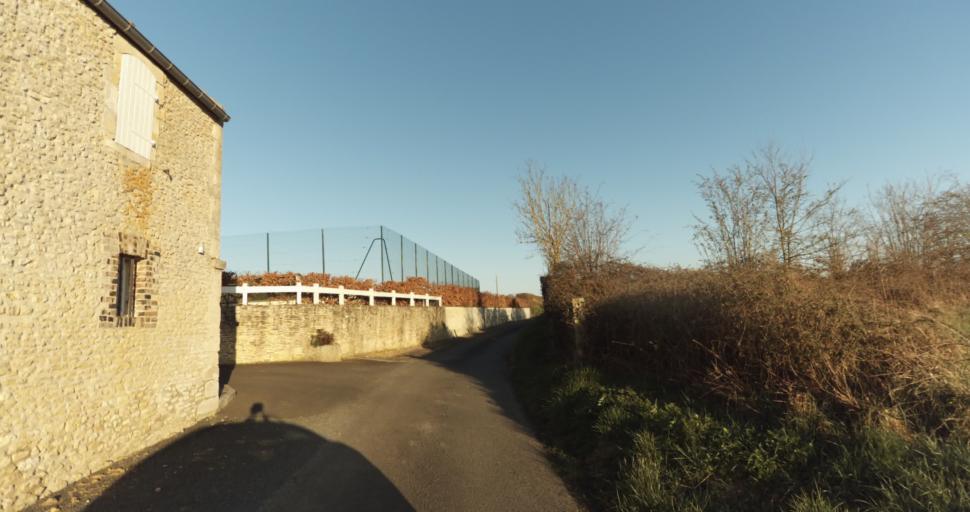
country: FR
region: Lower Normandy
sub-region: Departement du Calvados
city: Saint-Pierre-sur-Dives
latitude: 49.0241
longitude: -0.0111
